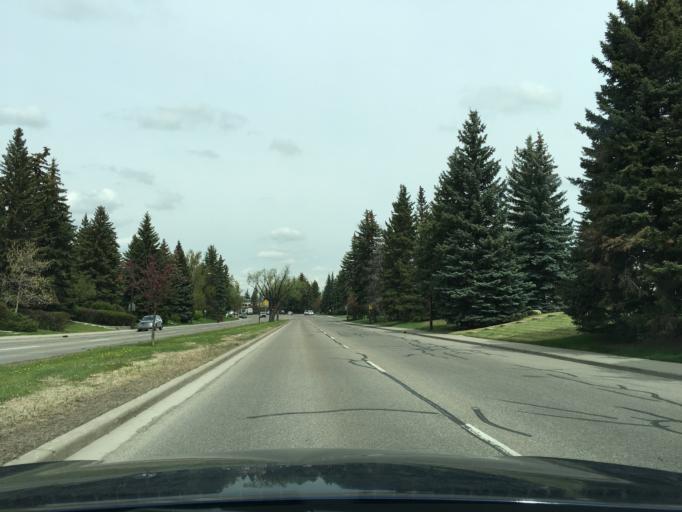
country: CA
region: Alberta
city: Calgary
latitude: 50.9446
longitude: -114.0855
